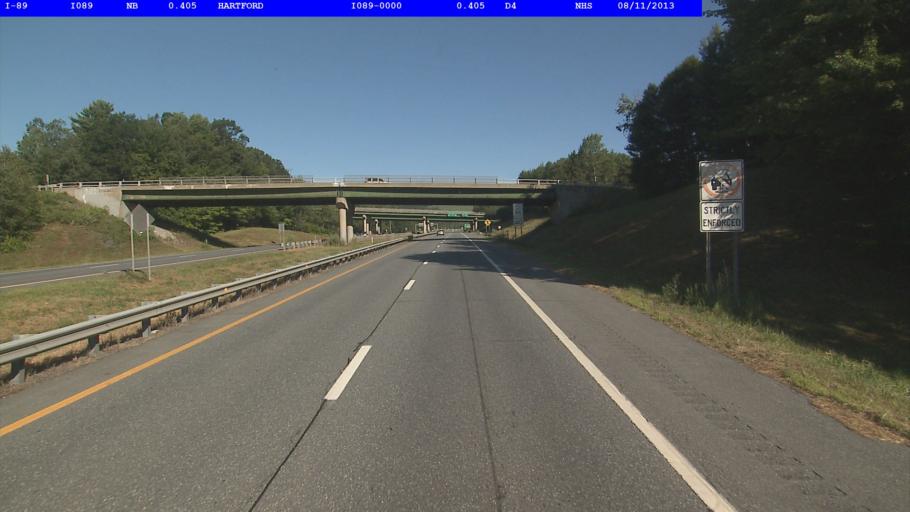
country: US
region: Vermont
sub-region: Windsor County
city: White River Junction
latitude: 43.6384
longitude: -72.3358
